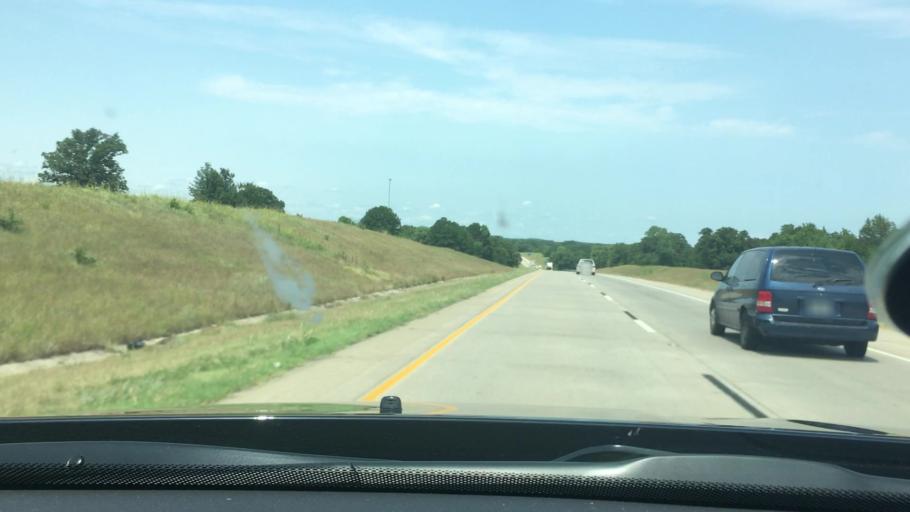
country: US
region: Oklahoma
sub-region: Love County
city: Marietta
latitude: 34.0011
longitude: -97.1409
